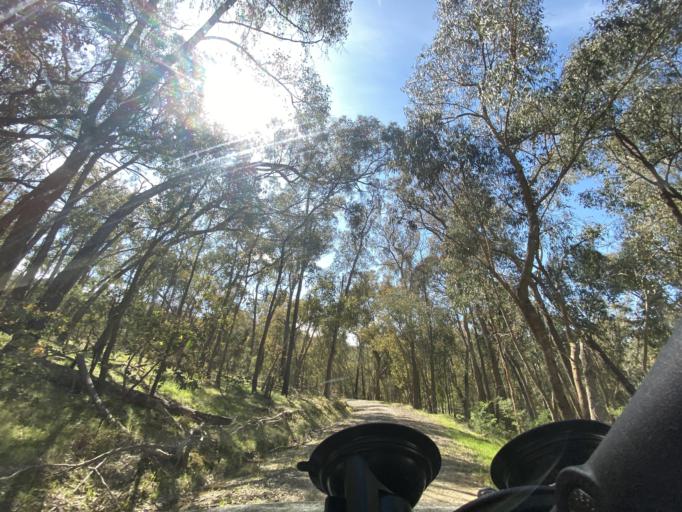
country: AU
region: Victoria
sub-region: Mansfield
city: Mansfield
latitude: -36.8019
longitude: 146.1185
